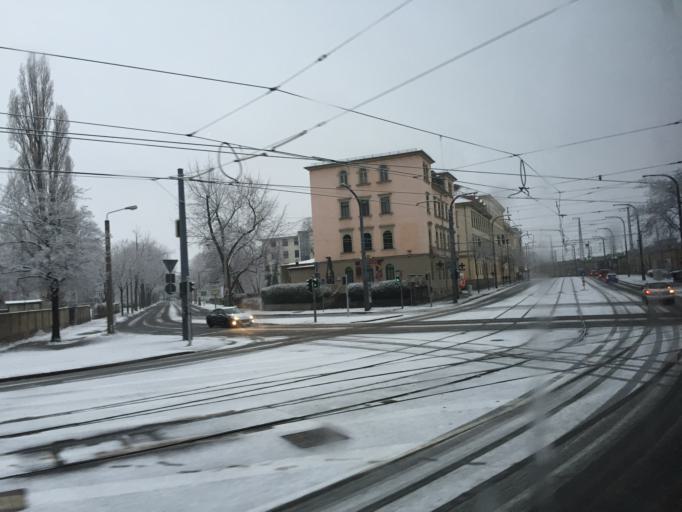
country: DE
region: Saxony
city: Dresden
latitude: 51.0648
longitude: 13.7409
